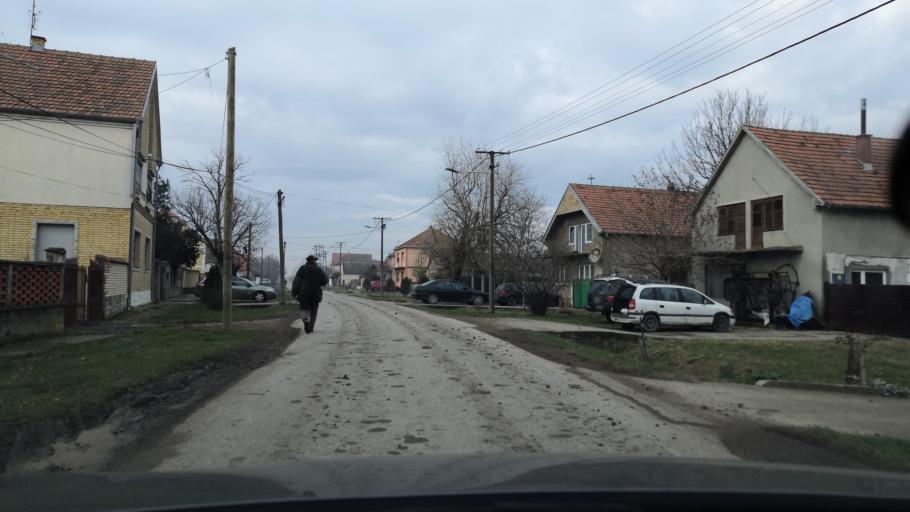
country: RS
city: Ugrinovci
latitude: 44.8872
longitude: 20.1461
